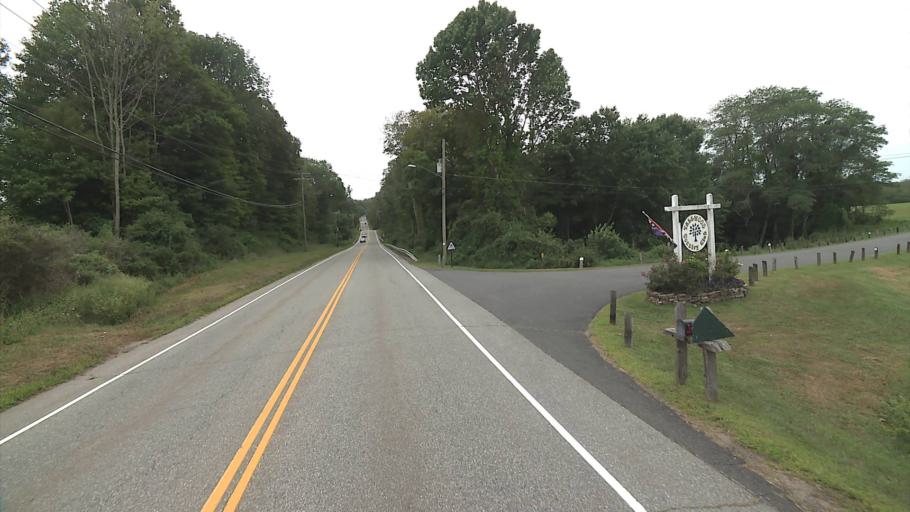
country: US
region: Connecticut
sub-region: Hartford County
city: Terramuggus
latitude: 41.6990
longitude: -72.4361
